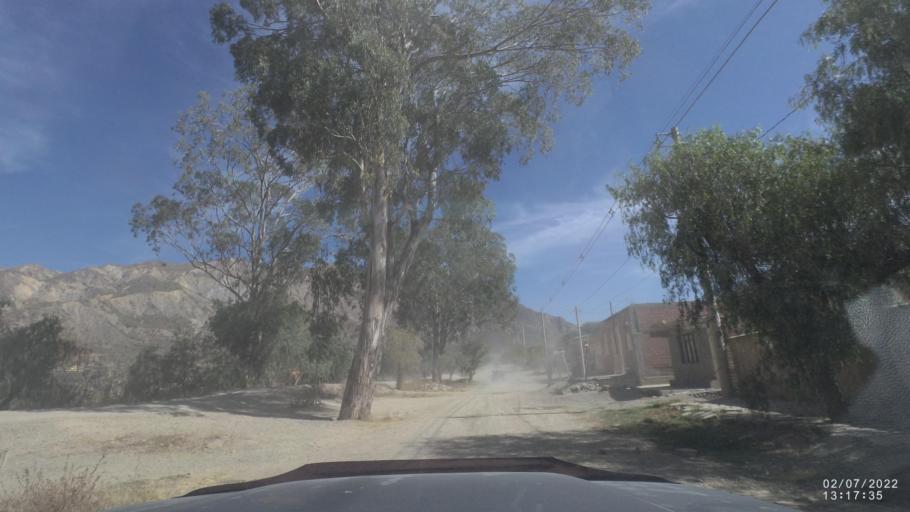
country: BO
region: Cochabamba
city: Irpa Irpa
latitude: -17.7328
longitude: -66.3098
